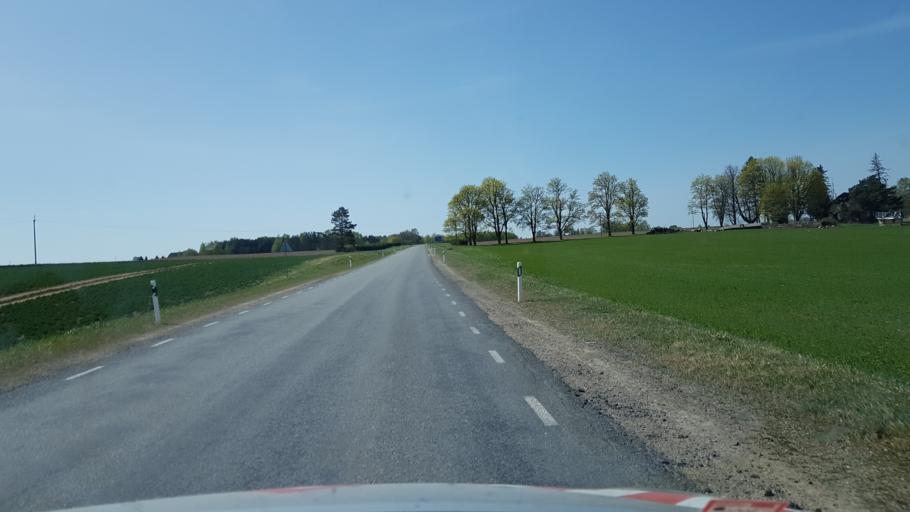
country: EE
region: Tartu
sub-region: Elva linn
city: Elva
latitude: 58.1912
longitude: 26.3599
